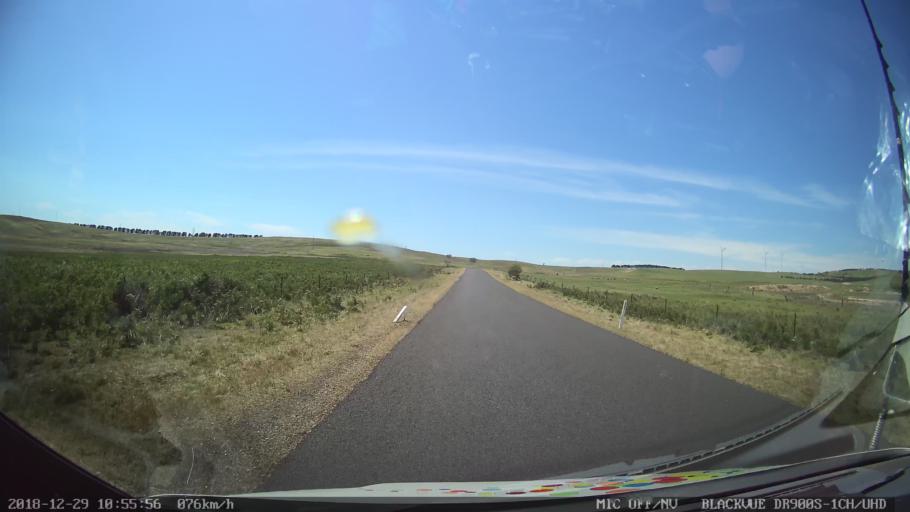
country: AU
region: New South Wales
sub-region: Palerang
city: Bungendore
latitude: -35.1294
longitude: 149.5346
